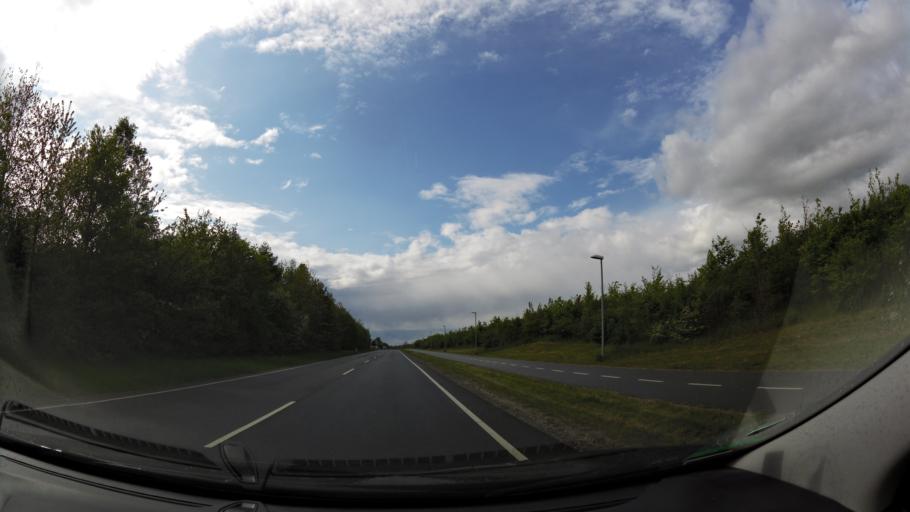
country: DK
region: South Denmark
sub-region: Nyborg Kommune
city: Nyborg
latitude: 55.3139
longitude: 10.7619
